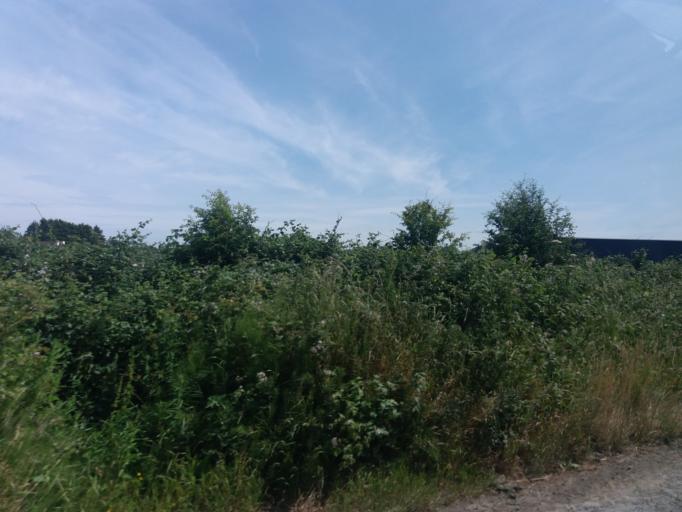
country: IE
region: Leinster
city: Lusk
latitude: 53.5364
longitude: -6.1978
